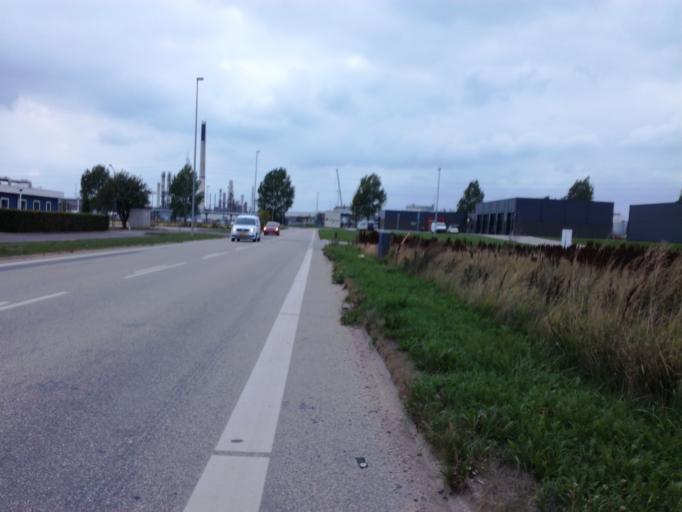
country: DK
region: South Denmark
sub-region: Fredericia Kommune
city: Fredericia
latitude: 55.5930
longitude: 9.7588
